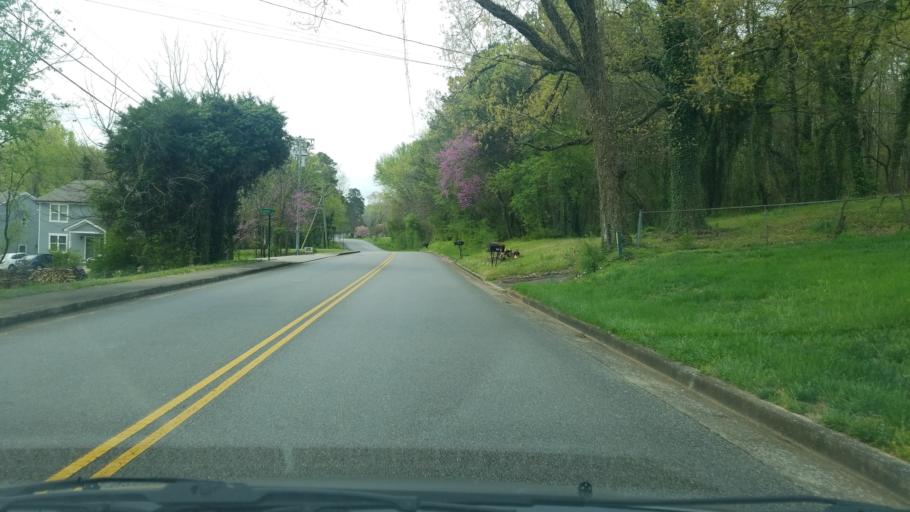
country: US
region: Tennessee
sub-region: Hamilton County
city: Collegedale
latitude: 35.0385
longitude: -85.0568
